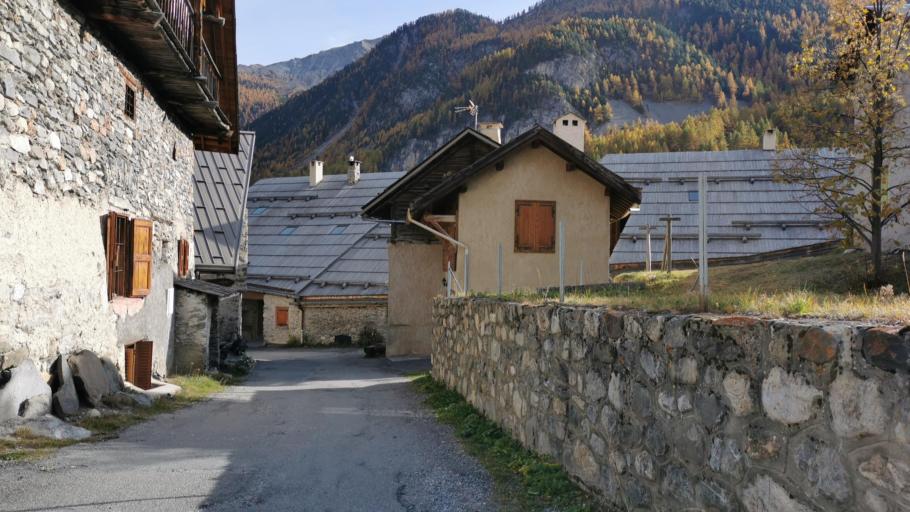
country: FR
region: Provence-Alpes-Cote d'Azur
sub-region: Departement des Hautes-Alpes
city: Villeneuve
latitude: 45.0188
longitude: 6.6034
